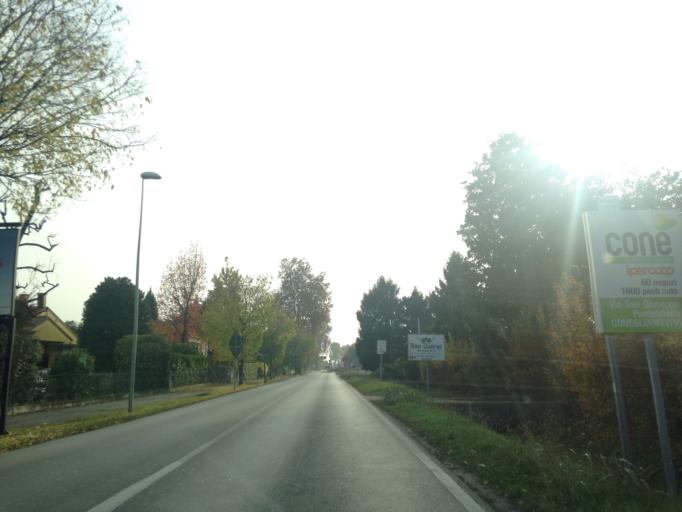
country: IT
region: Veneto
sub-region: Provincia di Treviso
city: Oderzo
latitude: 45.7698
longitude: 12.4879
